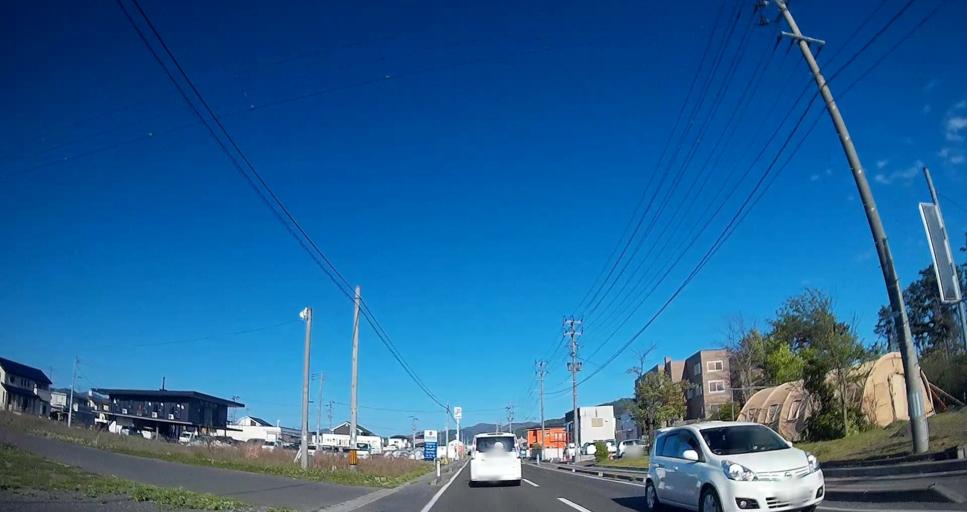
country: JP
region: Miyagi
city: Ishinomaki
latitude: 38.4168
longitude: 141.3539
